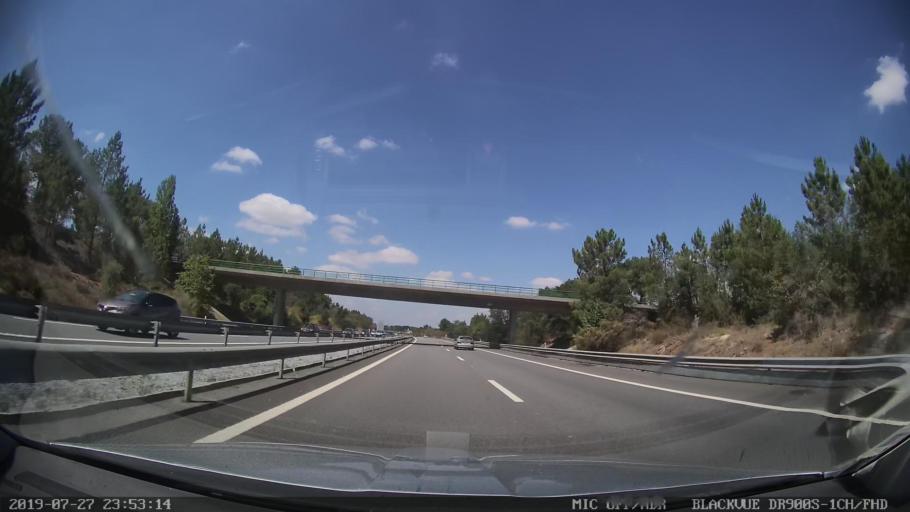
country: PT
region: Setubal
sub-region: Setubal
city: Setubal
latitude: 38.5996
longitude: -8.6834
